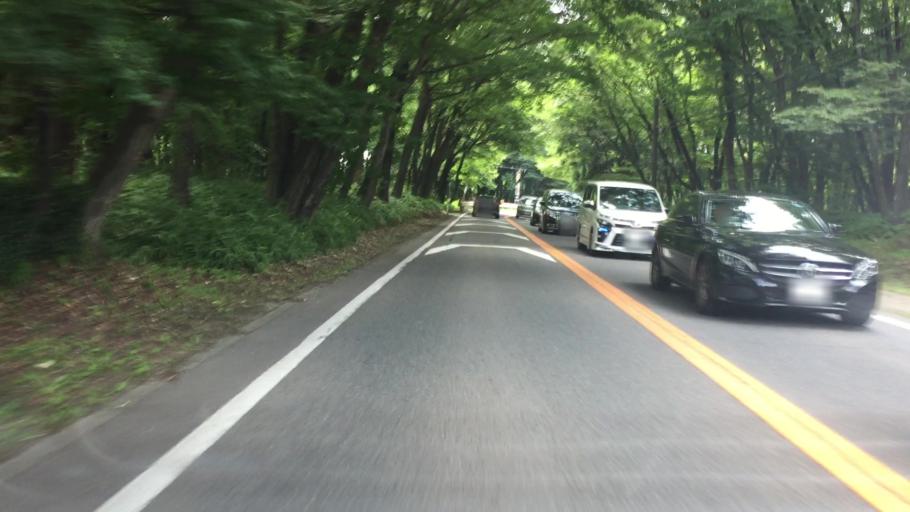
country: JP
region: Tochigi
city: Kuroiso
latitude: 37.0279
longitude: 140.0234
